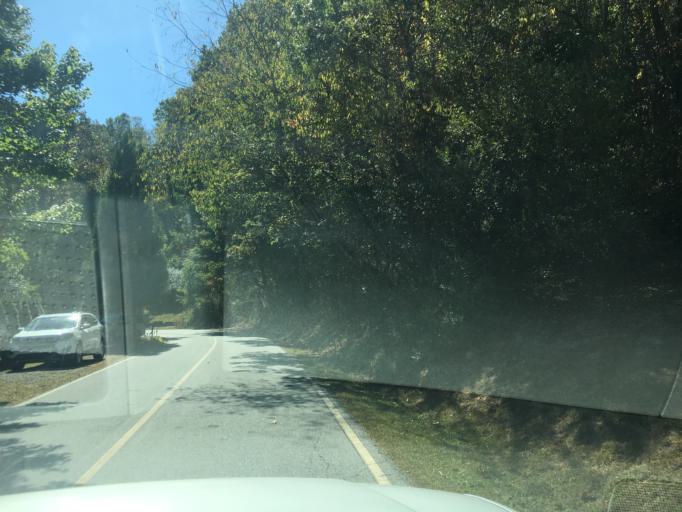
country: US
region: North Carolina
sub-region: Buncombe County
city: Woodfin
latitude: 35.6496
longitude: -82.5851
